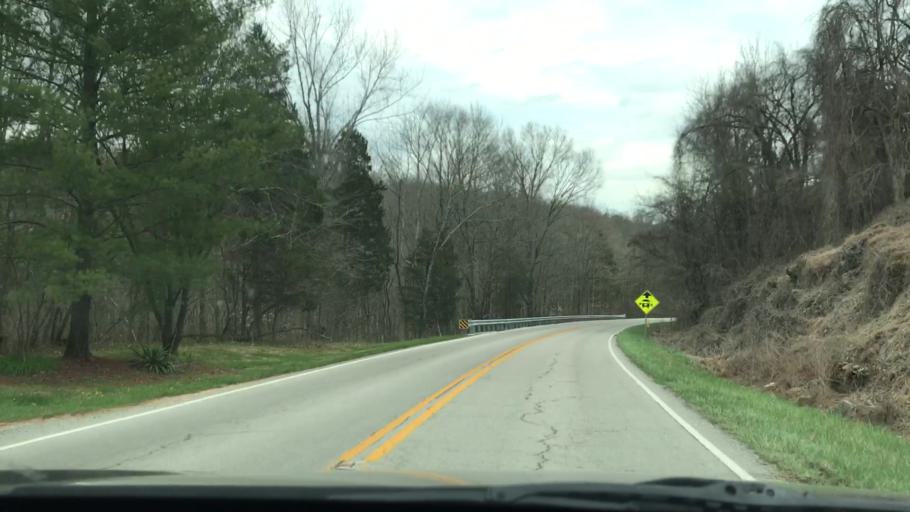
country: US
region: Kentucky
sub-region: Hart County
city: Munfordville
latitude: 37.3264
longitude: -85.7633
